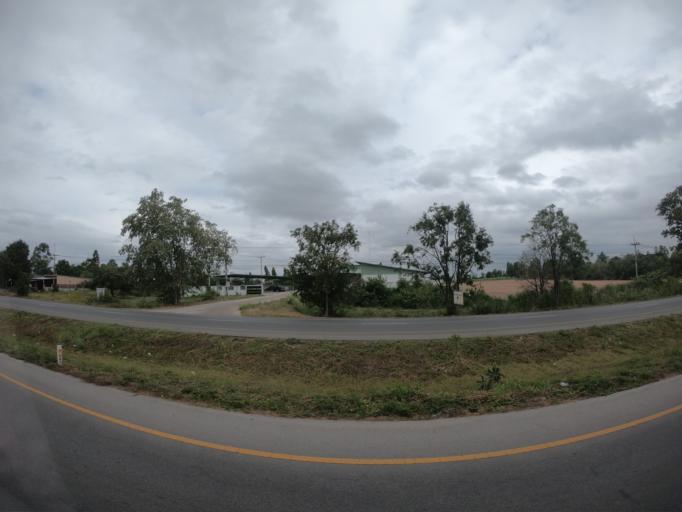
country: TH
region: Khon Kaen
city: Ban Phai
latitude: 16.0444
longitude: 102.8584
